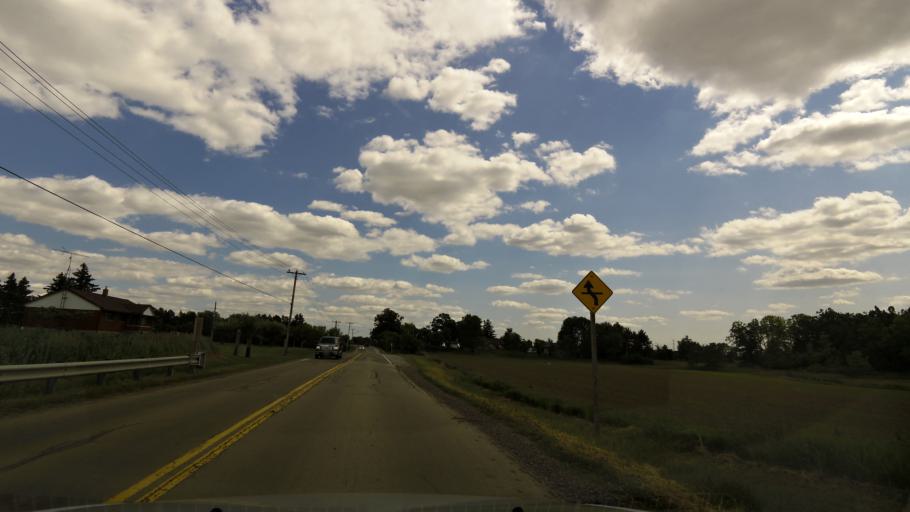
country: CA
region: Ontario
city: Ancaster
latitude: 43.1766
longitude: -80.0367
